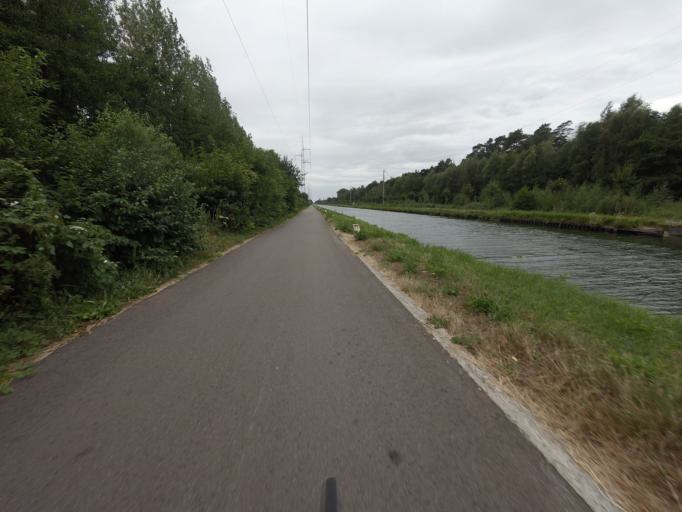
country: BE
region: Flanders
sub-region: Provincie Antwerpen
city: Brasschaat
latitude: 51.2866
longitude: 4.5393
